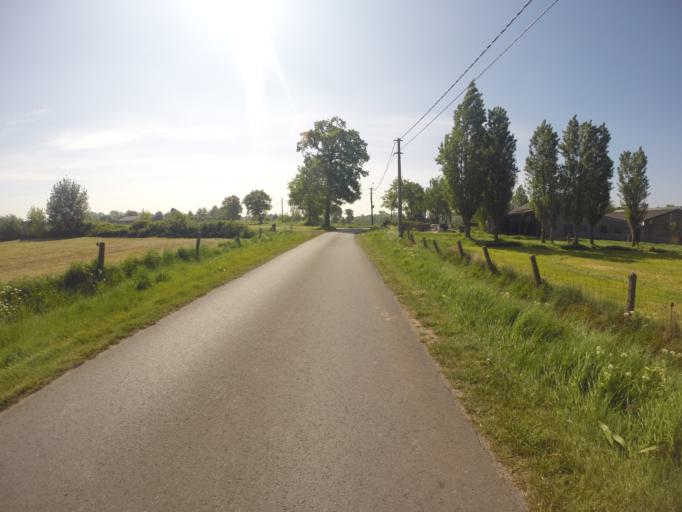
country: BE
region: Flanders
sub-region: Provincie West-Vlaanderen
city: Beernem
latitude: 51.1488
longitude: 3.3618
